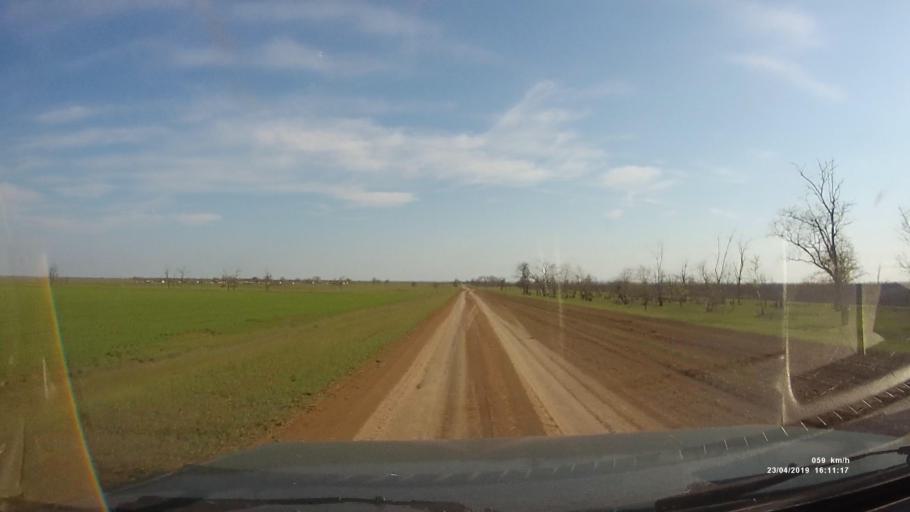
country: RU
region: Rostov
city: Remontnoye
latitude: 46.4752
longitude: 43.1231
